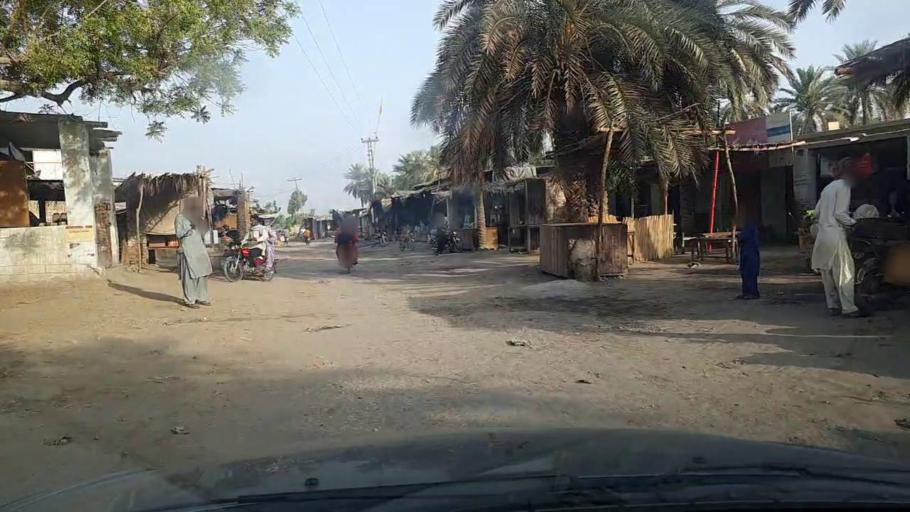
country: PK
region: Sindh
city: Pir jo Goth
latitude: 27.5577
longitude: 68.6750
